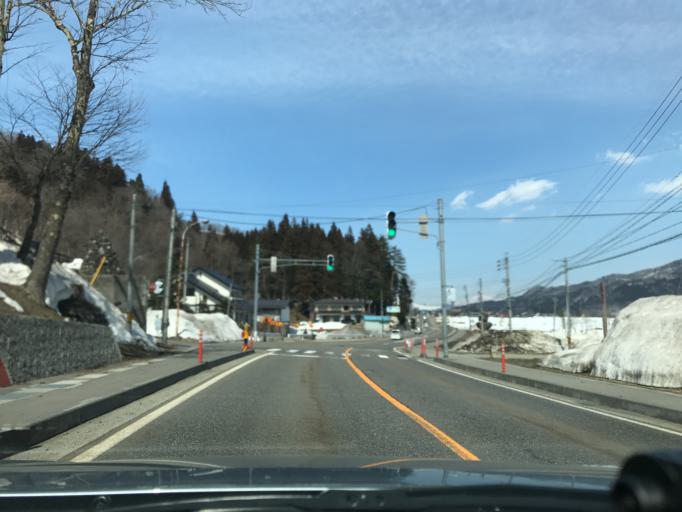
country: JP
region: Nagano
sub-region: Kitaazumi Gun
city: Hakuba
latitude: 36.6461
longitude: 137.8443
